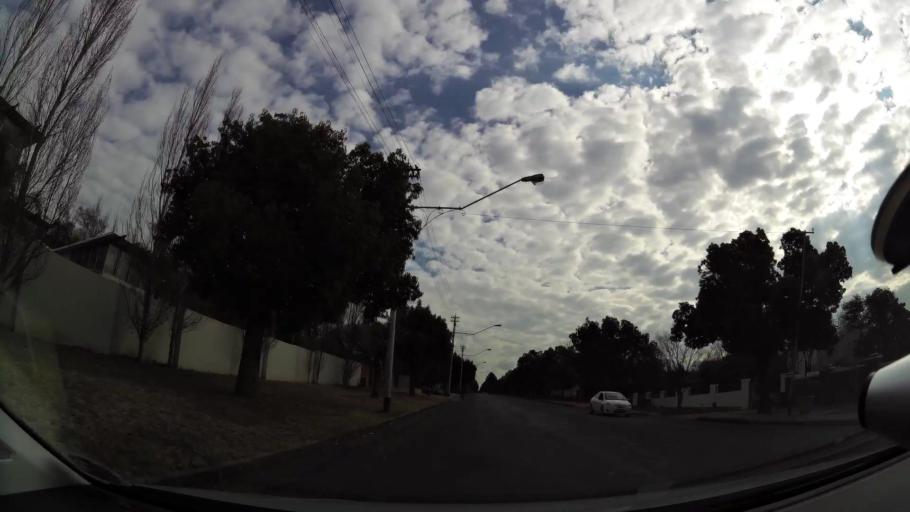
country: ZA
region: Orange Free State
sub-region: Mangaung Metropolitan Municipality
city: Bloemfontein
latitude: -29.0918
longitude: 26.2437
